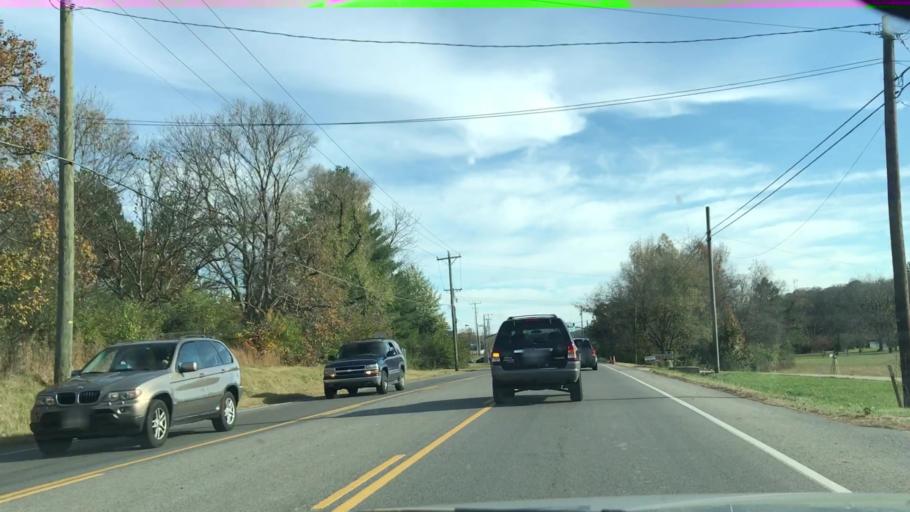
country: US
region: Tennessee
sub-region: Williamson County
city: Nolensville
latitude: 36.0005
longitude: -86.6947
